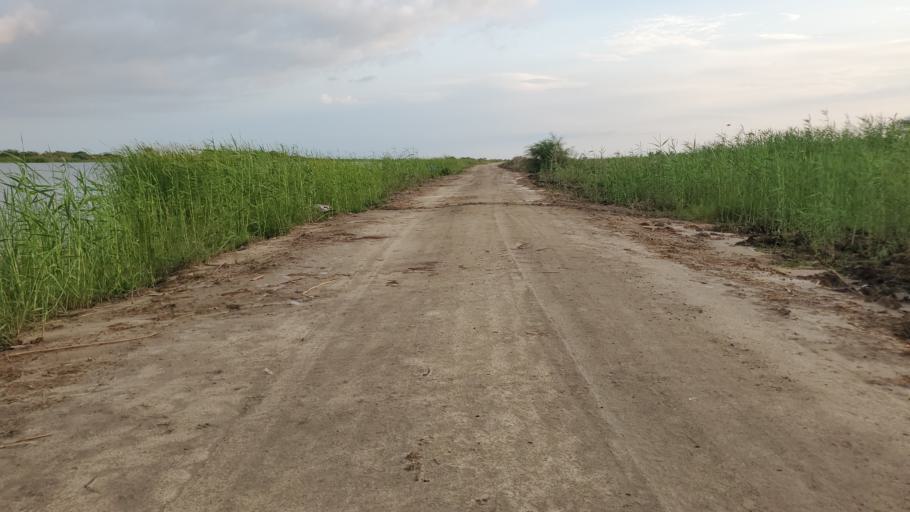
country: SN
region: Saint-Louis
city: Saint-Louis
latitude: 16.0127
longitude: -16.4006
